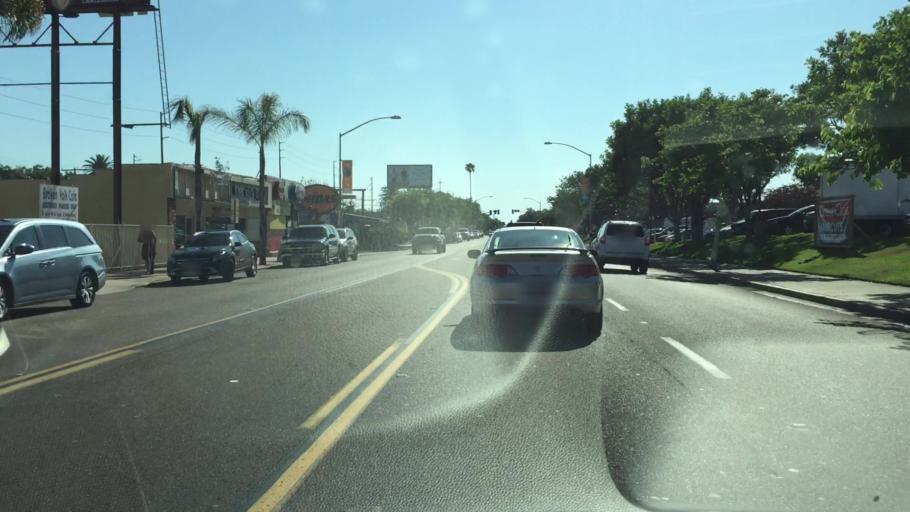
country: US
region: California
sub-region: San Diego County
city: La Jolla
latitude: 32.8008
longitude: -117.2364
